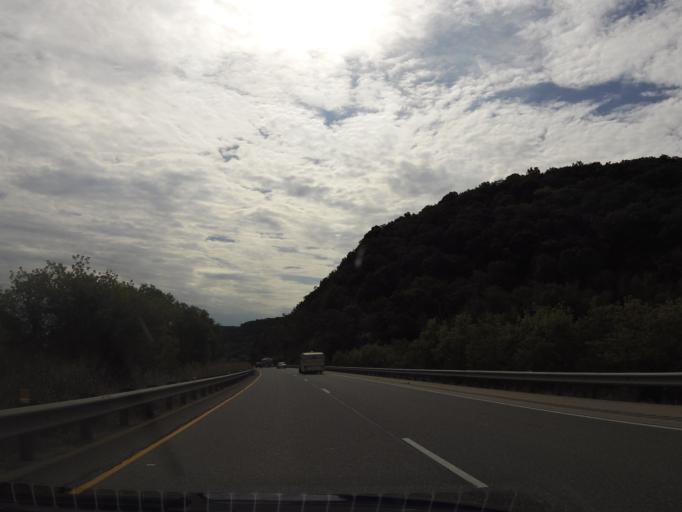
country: US
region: Wisconsin
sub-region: Trempealeau County
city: Trempealeau
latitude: 43.9280
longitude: -91.4118
